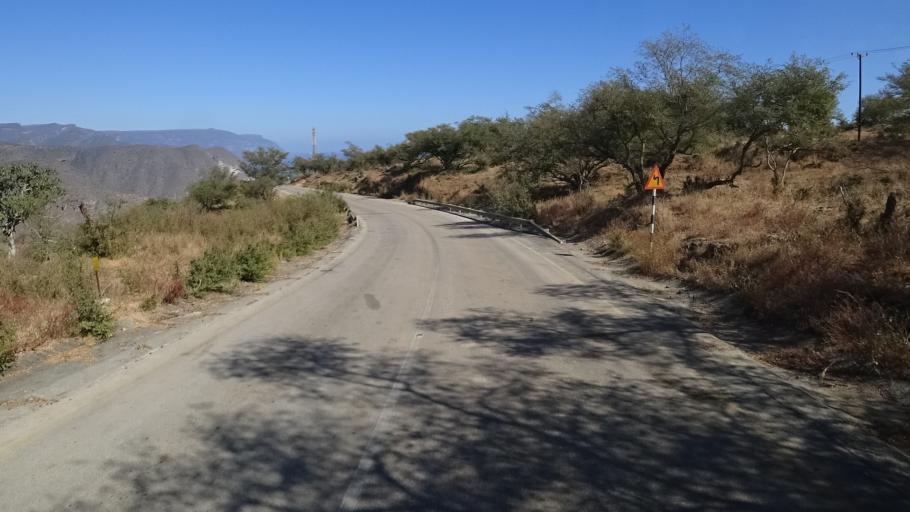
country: YE
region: Al Mahrah
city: Hawf
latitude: 16.7457
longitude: 53.3978
